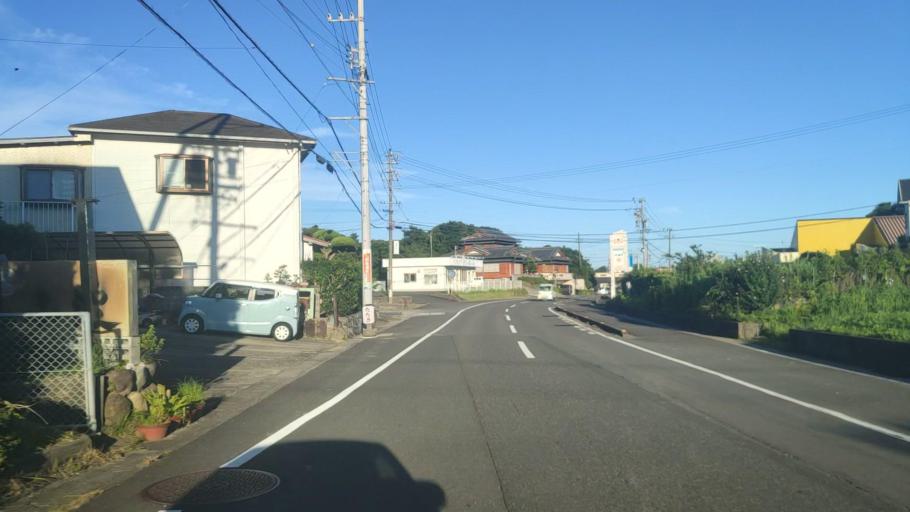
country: JP
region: Mie
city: Toba
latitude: 34.2567
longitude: 136.8221
